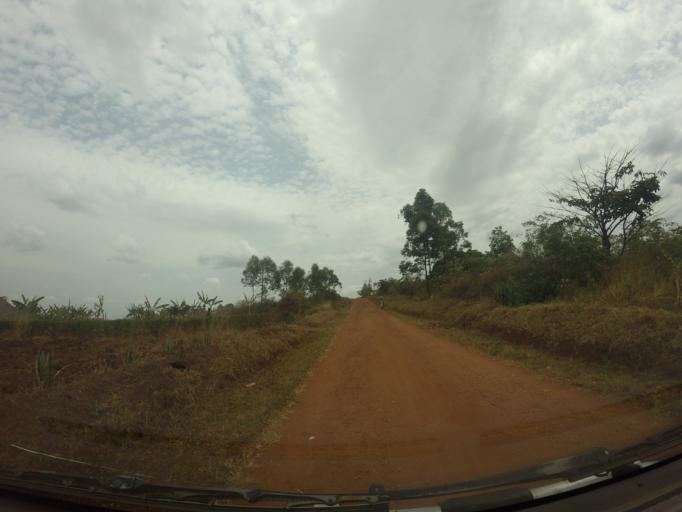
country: UG
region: Northern Region
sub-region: Arua District
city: Arua
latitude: 2.8238
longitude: 30.9048
